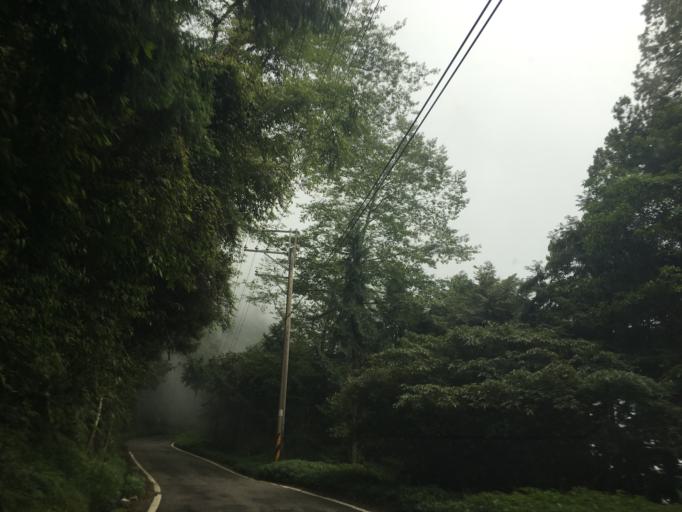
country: TW
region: Taiwan
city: Fengyuan
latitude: 24.2306
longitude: 120.9648
